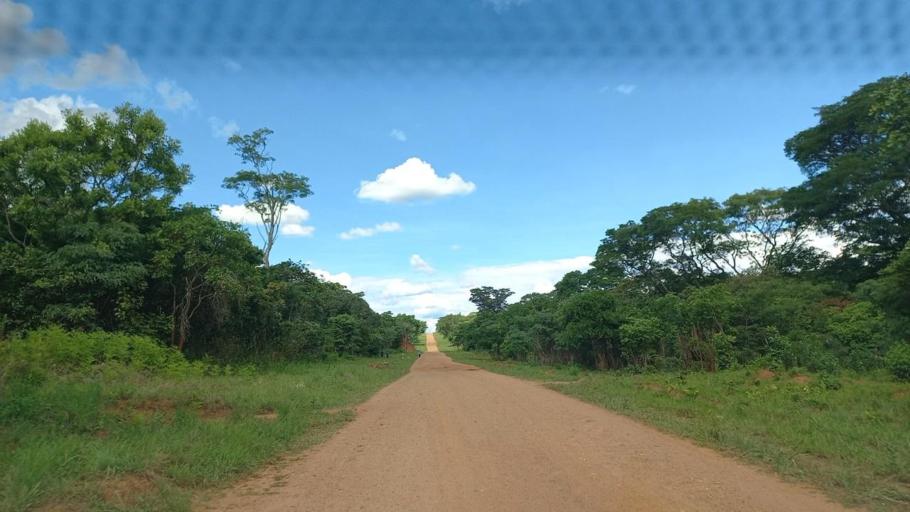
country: ZM
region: North-Western
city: Mwinilunga
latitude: -12.1152
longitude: 24.2812
